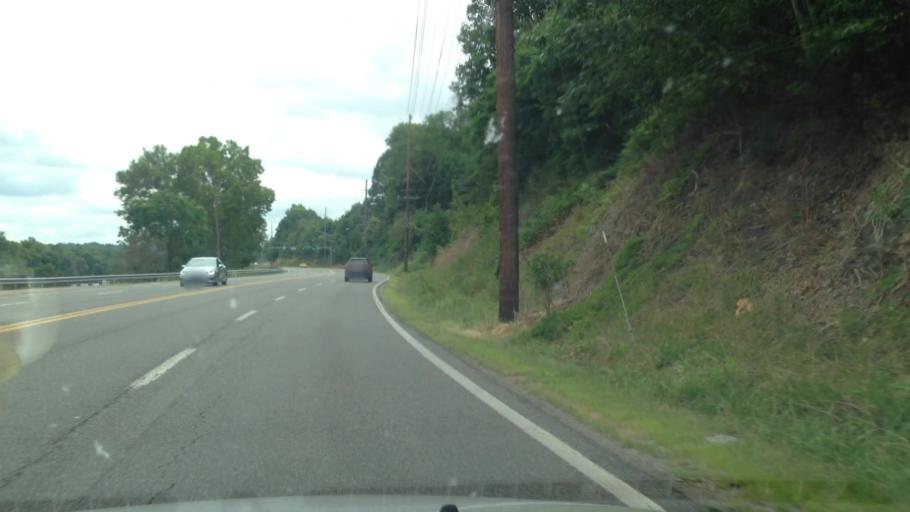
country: US
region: Virginia
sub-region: City of Danville
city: Danville
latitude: 36.5834
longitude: -79.4209
